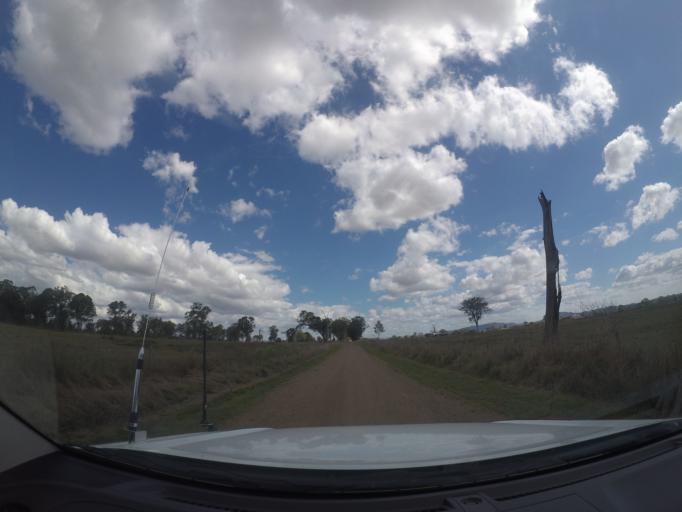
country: AU
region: Queensland
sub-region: Logan
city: Cedar Vale
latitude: -27.8912
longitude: 152.9595
